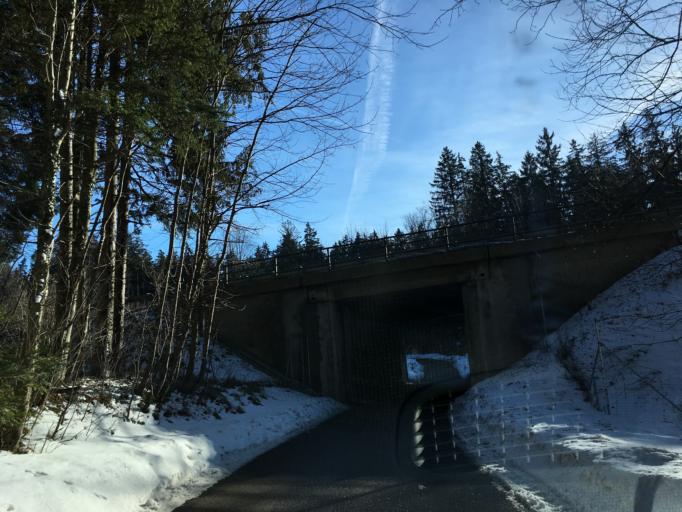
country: DE
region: Bavaria
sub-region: Upper Bavaria
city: Aschau im Chiemgau
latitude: 47.8057
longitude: 12.3279
